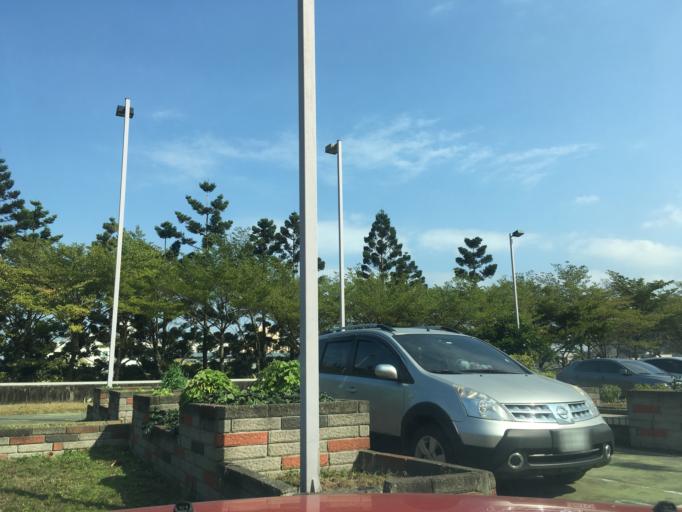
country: TW
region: Taiwan
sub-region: Hsinchu
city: Hsinchu
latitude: 24.7823
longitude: 120.9978
